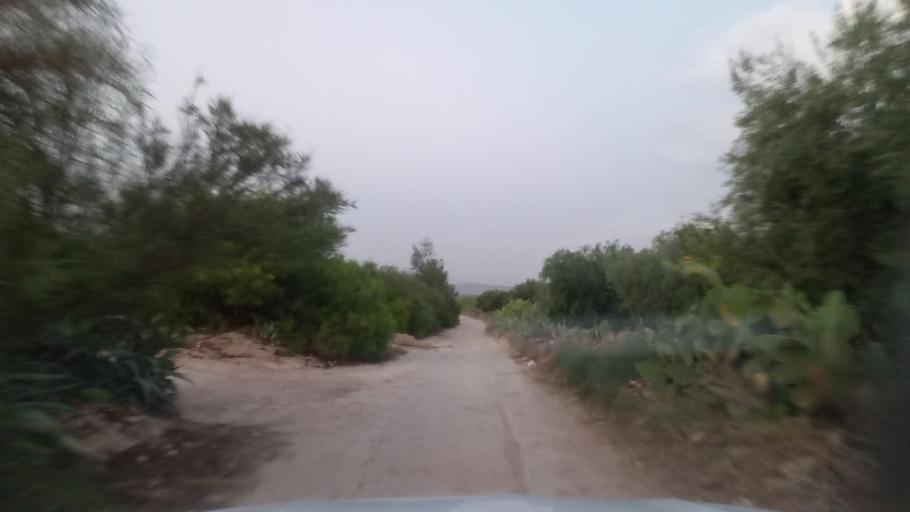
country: TN
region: Al Qasrayn
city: Kasserine
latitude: 35.2775
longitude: 9.0294
